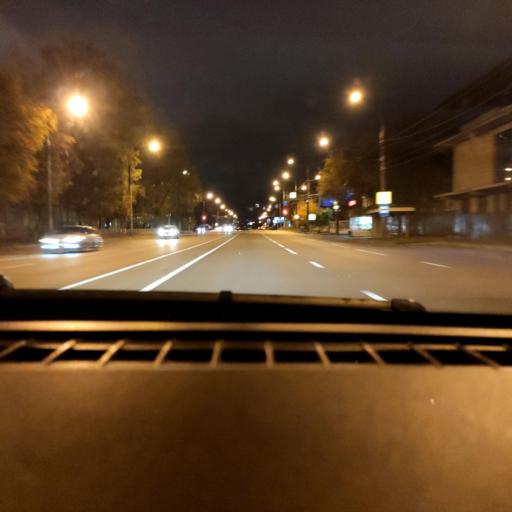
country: RU
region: Voronezj
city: Voronezh
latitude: 51.6711
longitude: 39.1592
